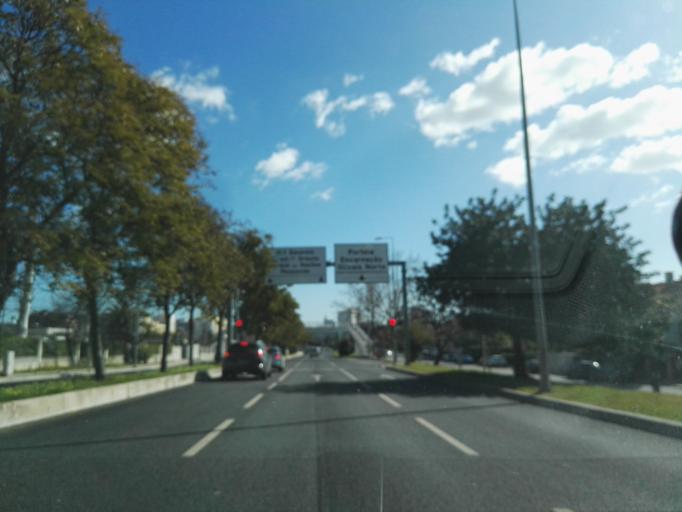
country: PT
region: Lisbon
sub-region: Loures
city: Moscavide
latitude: 38.7781
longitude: -9.1145
